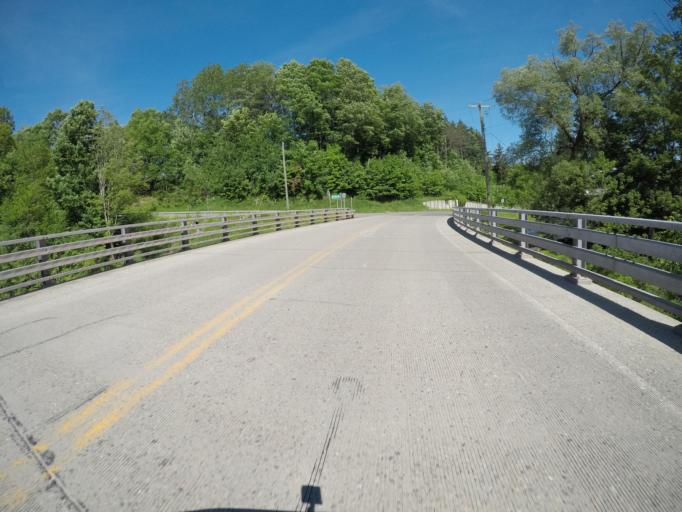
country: US
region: New York
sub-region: Delaware County
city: Delhi
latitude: 42.2018
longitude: -74.9687
